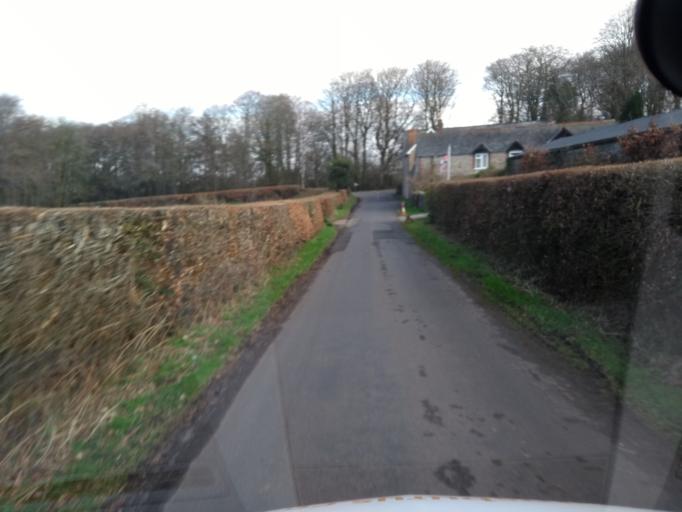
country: GB
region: England
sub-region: Somerset
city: Chard
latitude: 50.9224
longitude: -3.0331
